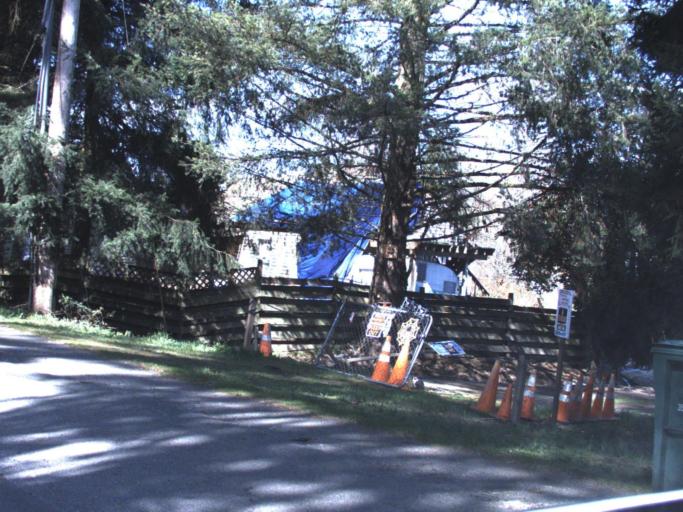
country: US
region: Washington
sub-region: King County
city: Lea Hill
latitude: 47.2740
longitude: -122.1518
